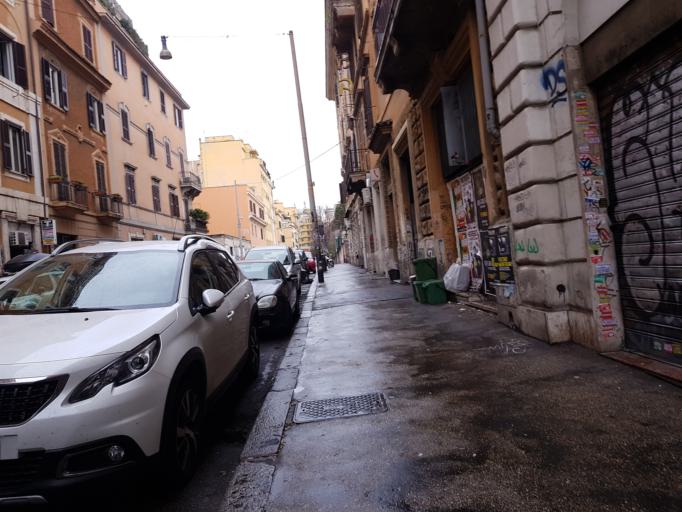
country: IT
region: Latium
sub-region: Citta metropolitana di Roma Capitale
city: Rome
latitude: 41.8986
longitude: 12.5168
